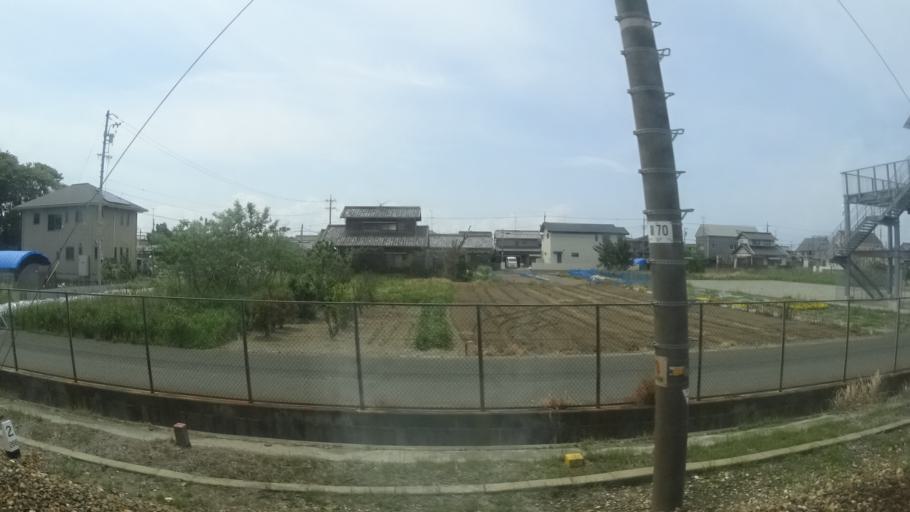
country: JP
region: Shizuoka
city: Hamamatsu
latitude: 34.6855
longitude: 137.6406
